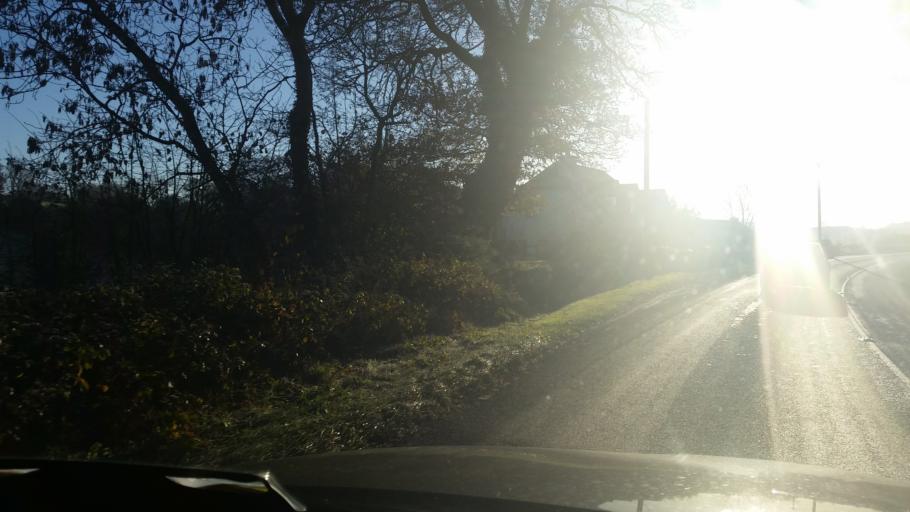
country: IE
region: Leinster
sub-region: Loch Garman
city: Gorey
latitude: 52.6485
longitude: -6.2905
